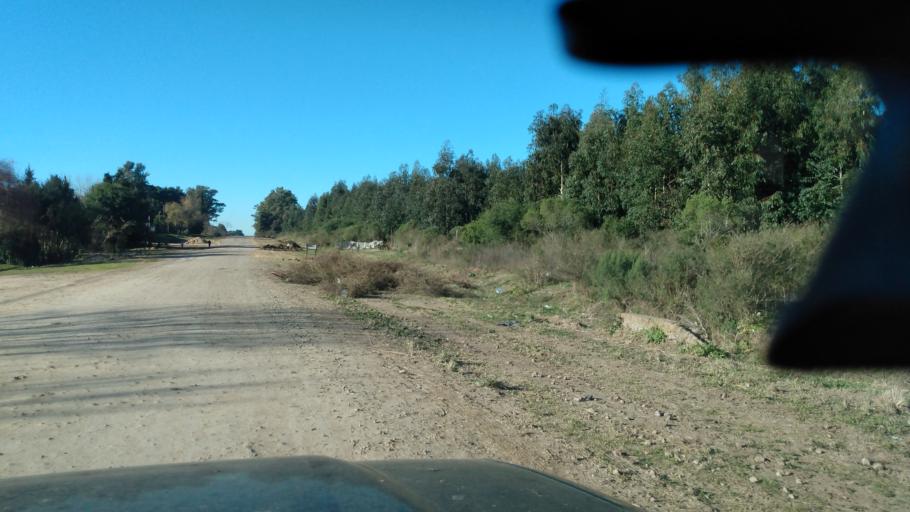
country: AR
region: Buenos Aires
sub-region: Partido de Lujan
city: Lujan
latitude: -34.5686
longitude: -59.1766
